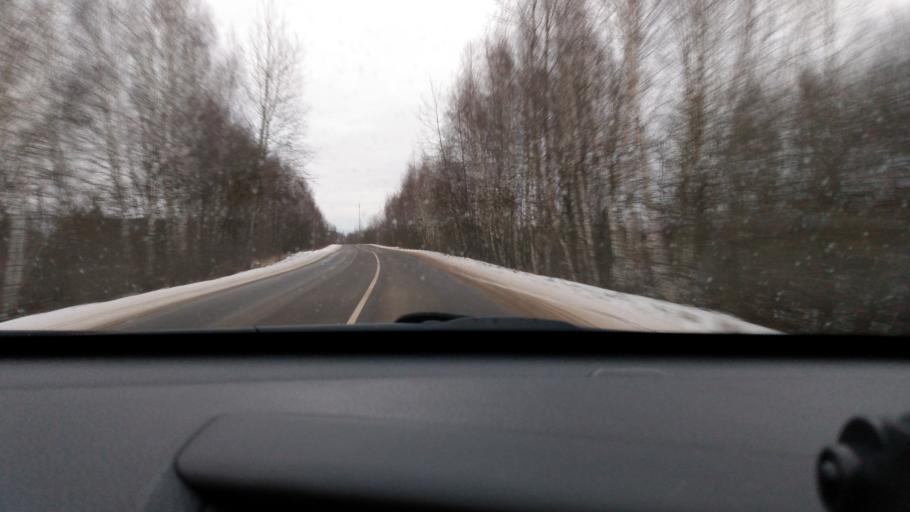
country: RU
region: Moskovskaya
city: Bronnitsy
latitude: 55.2908
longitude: 38.2401
